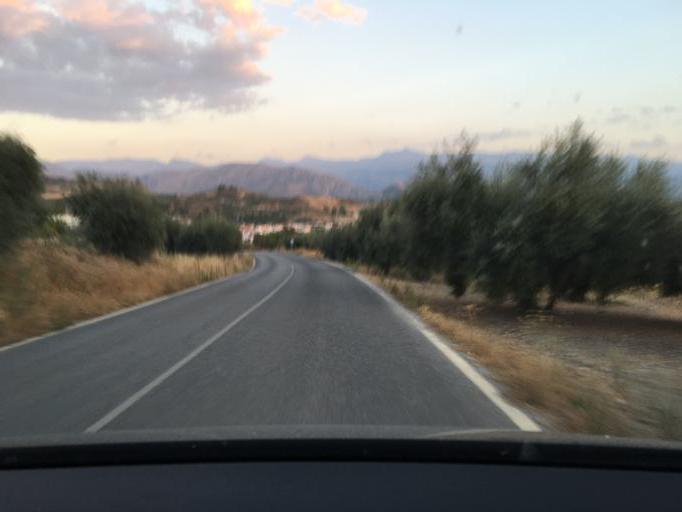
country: ES
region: Andalusia
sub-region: Provincia de Granada
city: Beas de Granada
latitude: 37.2254
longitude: -3.4897
